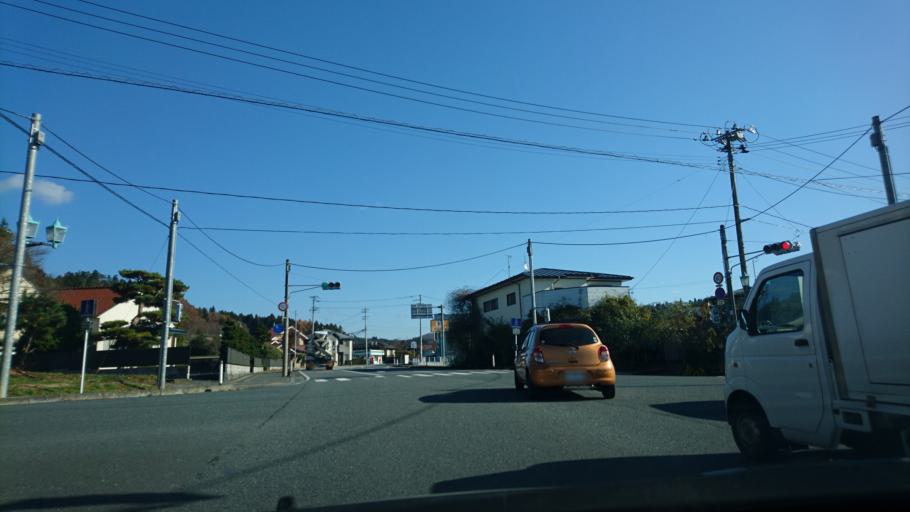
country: JP
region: Iwate
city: Ichinoseki
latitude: 38.9957
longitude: 141.3262
